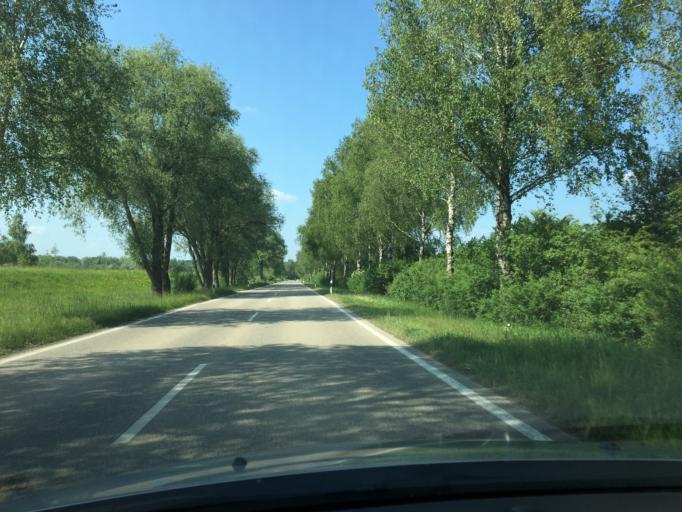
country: DE
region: Bavaria
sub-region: Upper Bavaria
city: Langenpreising
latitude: 48.4288
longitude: 11.9356
